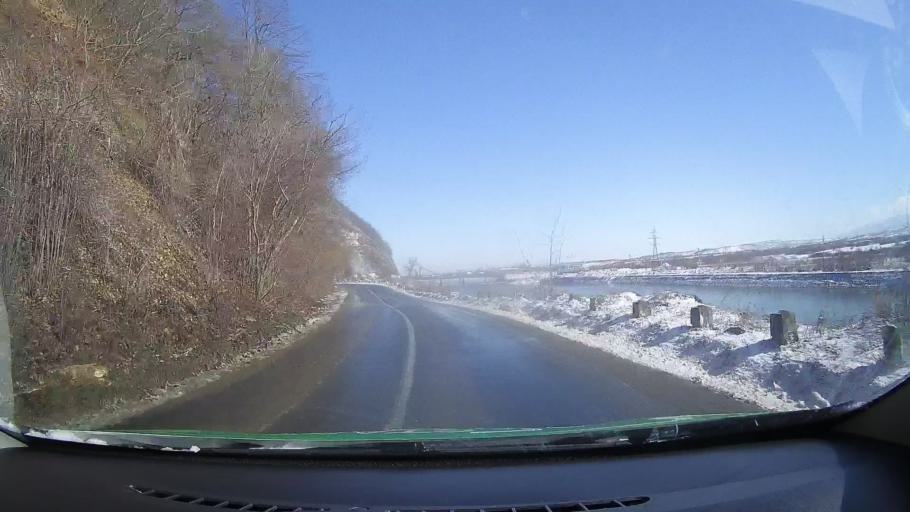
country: RO
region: Sibiu
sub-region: Comuna Turnu Rosu
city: Turnu Rosu
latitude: 45.6656
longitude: 24.3111
